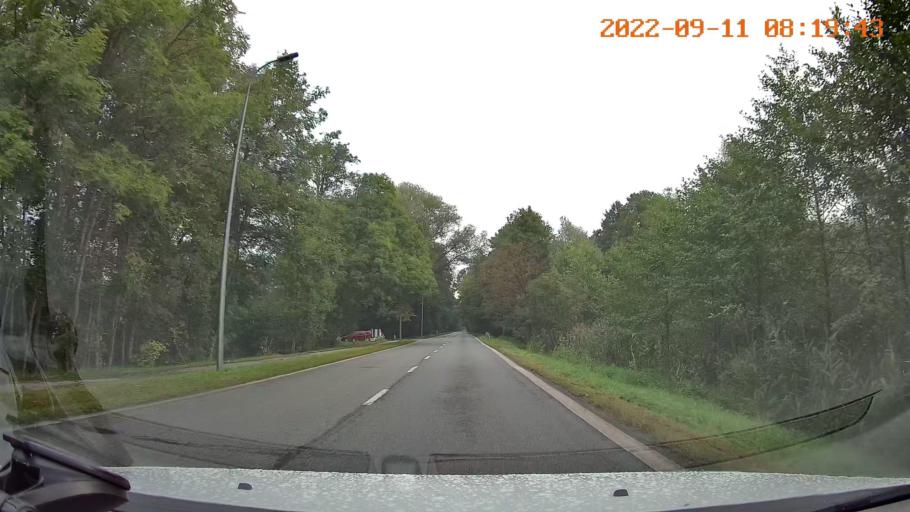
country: PL
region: Silesian Voivodeship
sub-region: Tychy
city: Tychy
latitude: 50.1535
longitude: 19.0068
